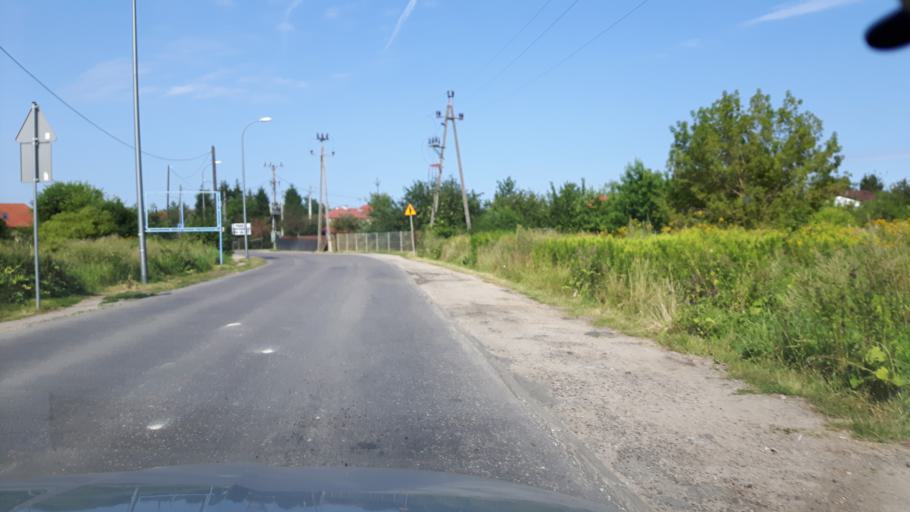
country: PL
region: Masovian Voivodeship
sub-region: Powiat wolominski
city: Marki
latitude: 52.3226
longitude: 21.0812
